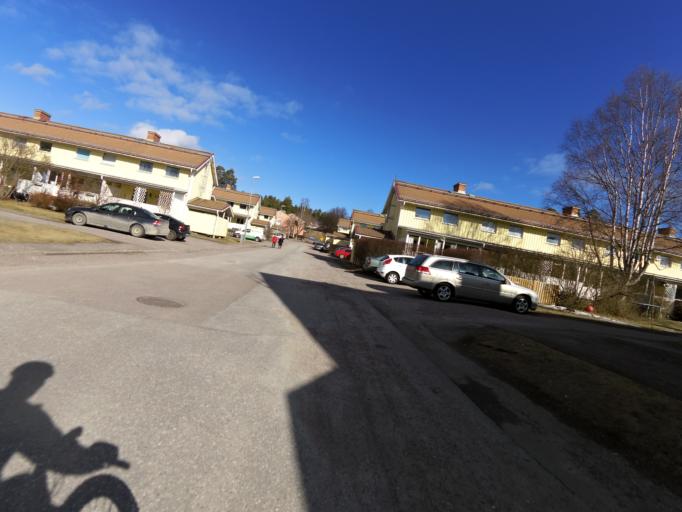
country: SE
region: Gaevleborg
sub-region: Hofors Kommun
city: Hofors
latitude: 60.5464
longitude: 16.2759
